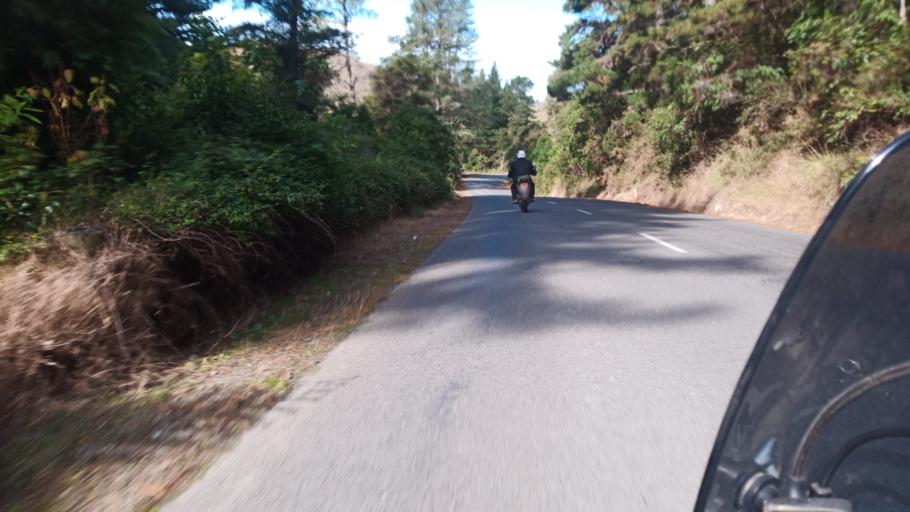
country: NZ
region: Hawke's Bay
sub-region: Wairoa District
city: Wairoa
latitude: -39.0380
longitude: 177.1069
